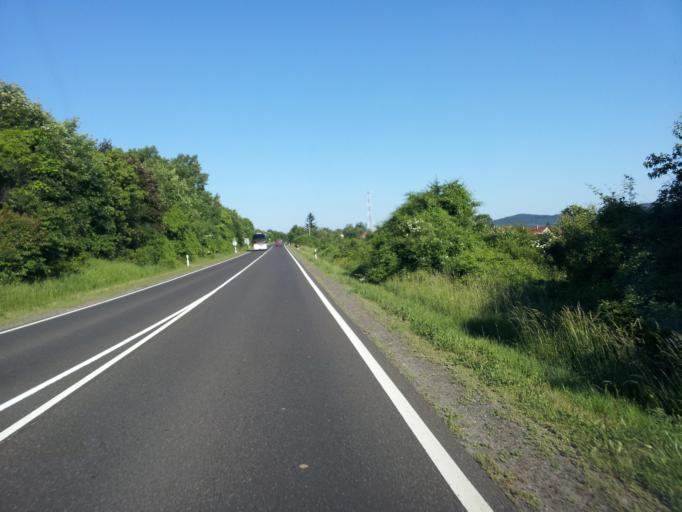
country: HU
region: Nograd
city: Nagyoroszi
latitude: 48.0481
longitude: 19.0410
